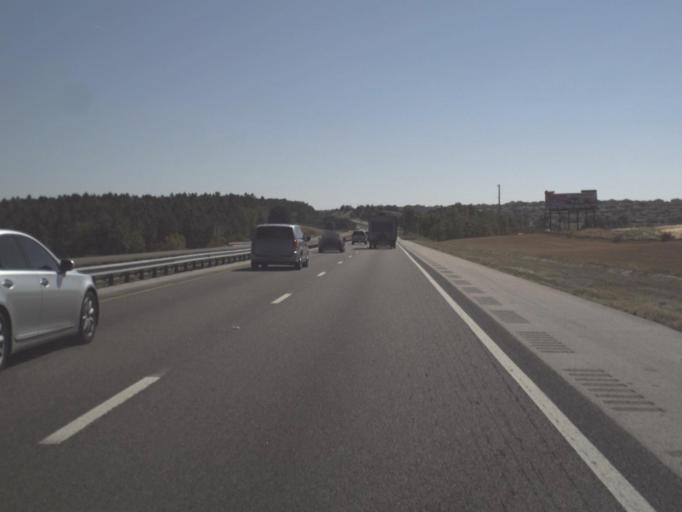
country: US
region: Florida
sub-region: Lake County
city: Montverde
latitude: 28.5822
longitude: -81.7054
